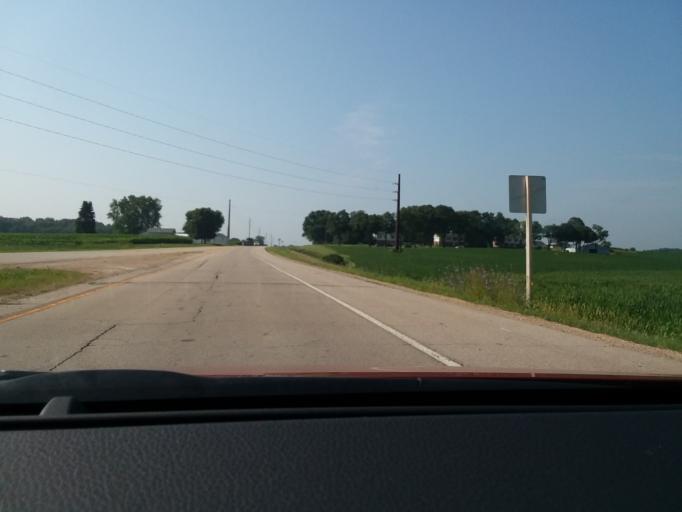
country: US
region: Wisconsin
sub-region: Dane County
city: Waunakee
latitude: 43.1862
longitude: -89.4118
